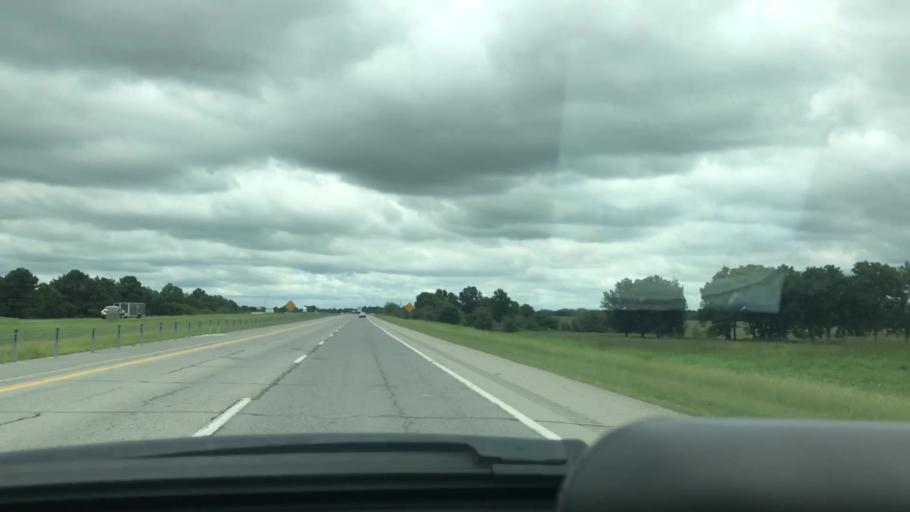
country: US
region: Oklahoma
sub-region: McIntosh County
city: Checotah
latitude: 35.5479
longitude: -95.5003
